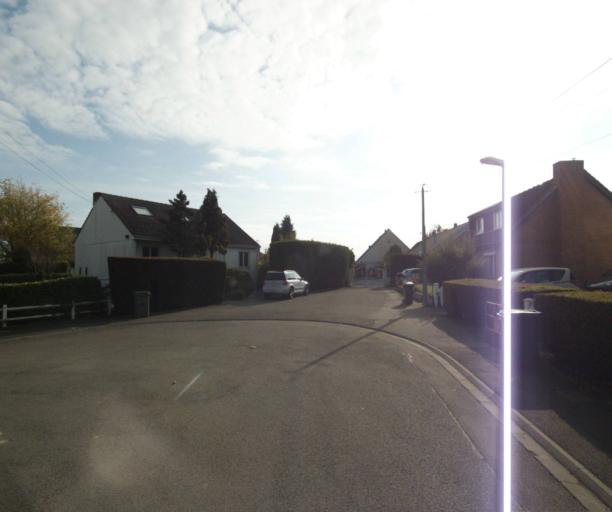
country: FR
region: Nord-Pas-de-Calais
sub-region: Departement du Nord
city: Lompret
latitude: 50.6655
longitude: 2.9935
